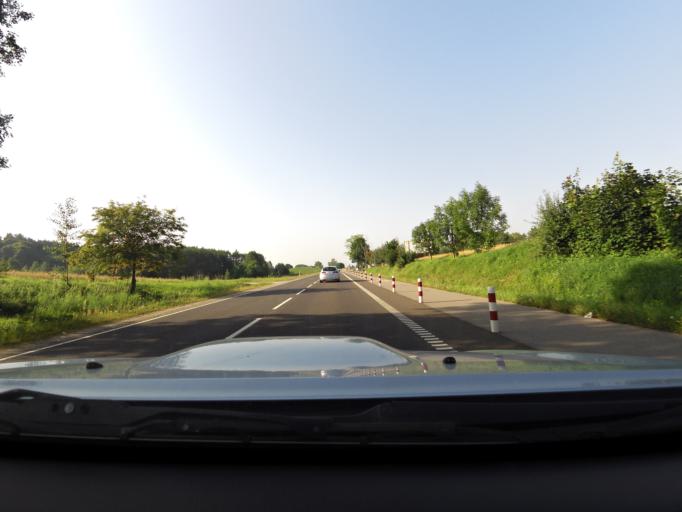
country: LT
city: Lazdijai
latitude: 54.1474
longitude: 23.4686
